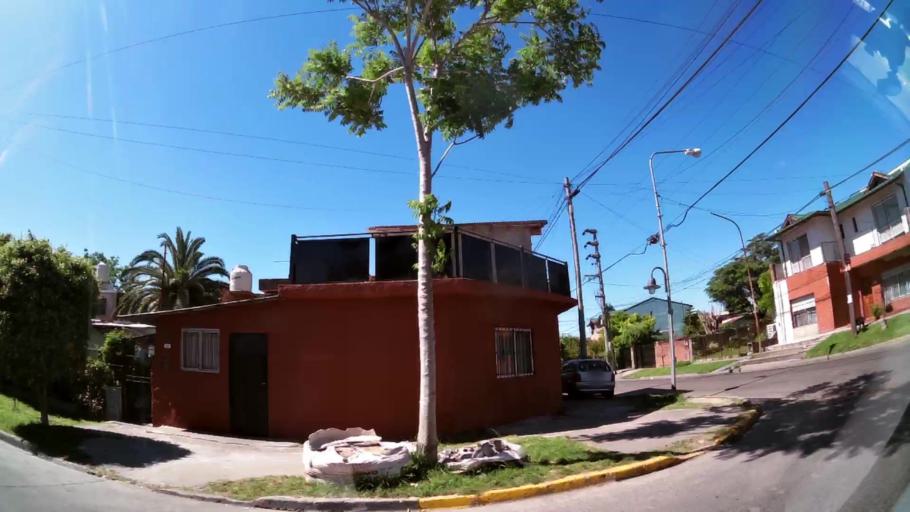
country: AR
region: Buenos Aires
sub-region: Partido de Tigre
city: Tigre
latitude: -34.4970
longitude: -58.6109
